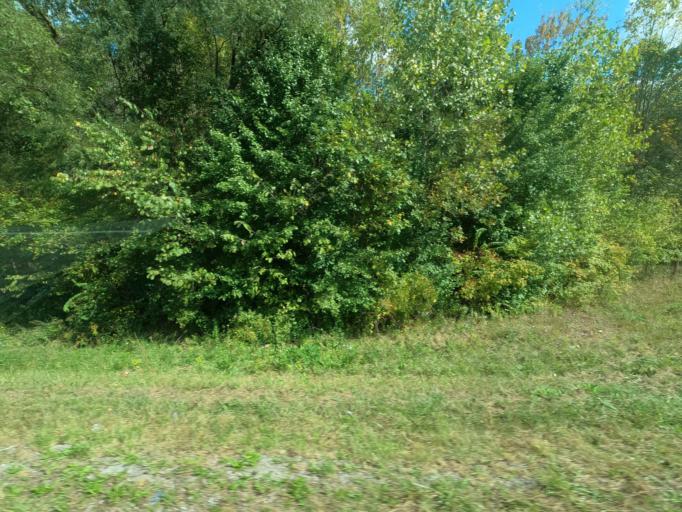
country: US
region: Illinois
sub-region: Johnson County
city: Vienna
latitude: 37.4232
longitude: -88.8931
